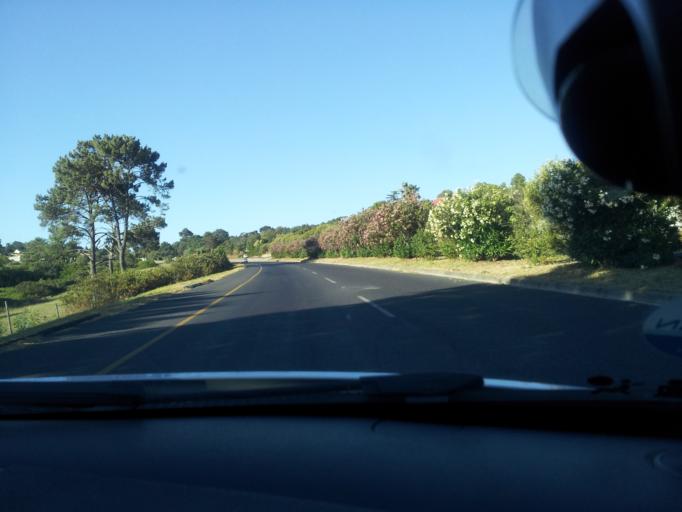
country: ZA
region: Western Cape
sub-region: Cape Winelands District Municipality
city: Stellenbosch
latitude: -34.0607
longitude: 18.8290
